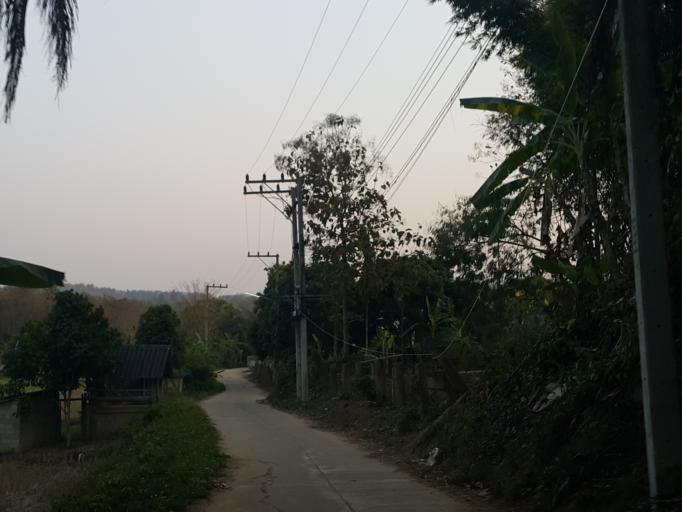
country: TH
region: Chiang Mai
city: Mae Taeng
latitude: 19.1113
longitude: 98.8282
